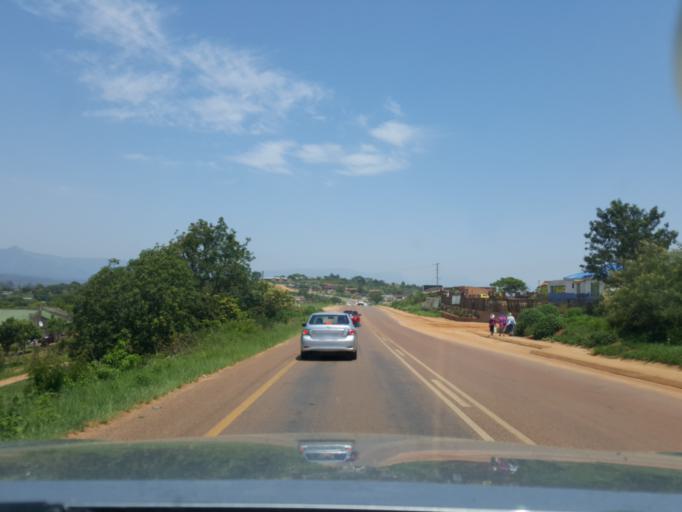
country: ZA
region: Limpopo
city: Thulamahashi
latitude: -24.8491
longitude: 31.1029
